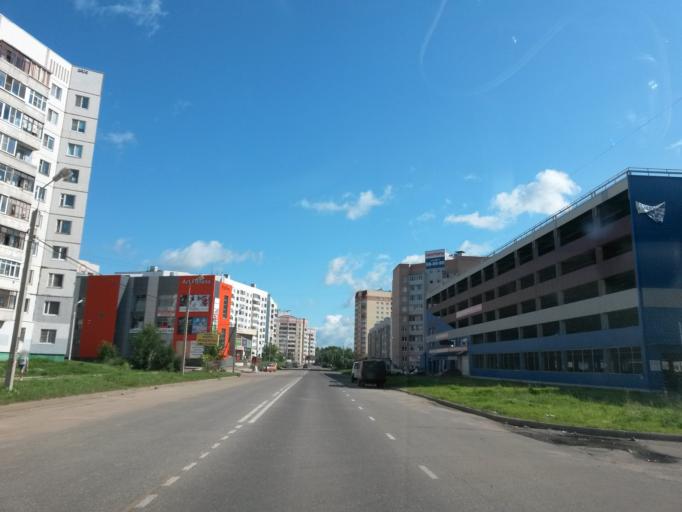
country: RU
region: Jaroslavl
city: Yaroslavl
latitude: 57.6934
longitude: 39.7795
